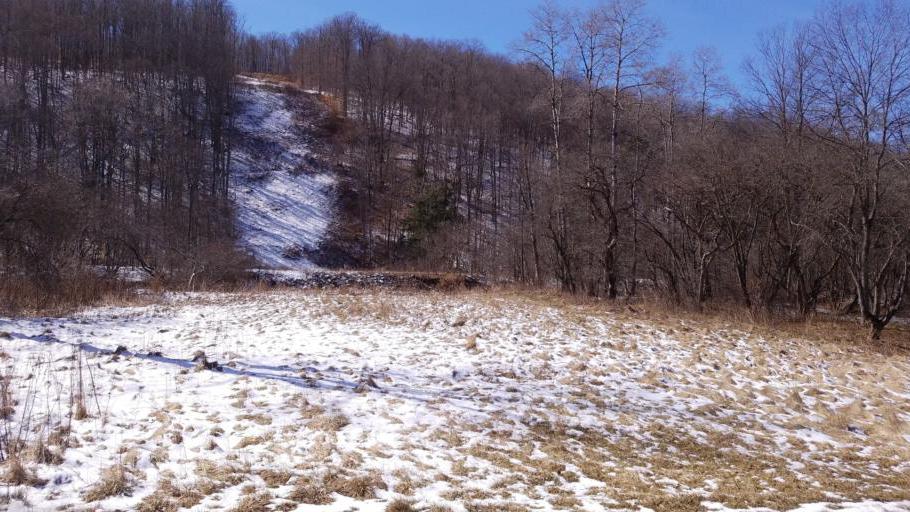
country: US
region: New York
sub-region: Allegany County
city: Andover
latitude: 41.9417
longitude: -77.8140
